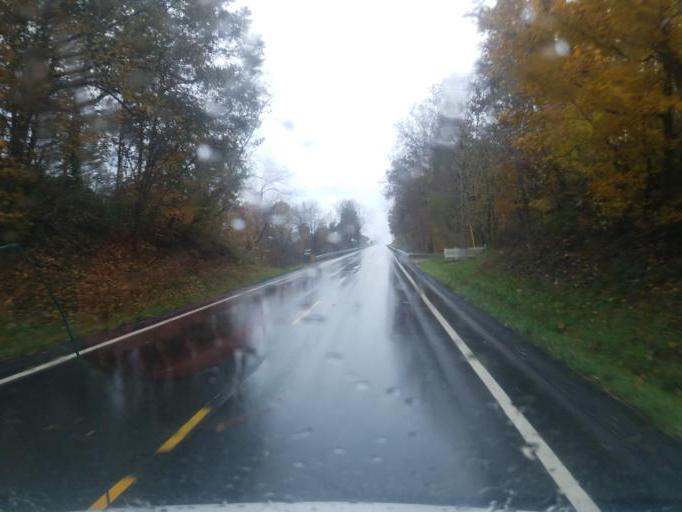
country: US
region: Ohio
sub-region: Washington County
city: Beverly
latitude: 39.4572
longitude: -81.6409
